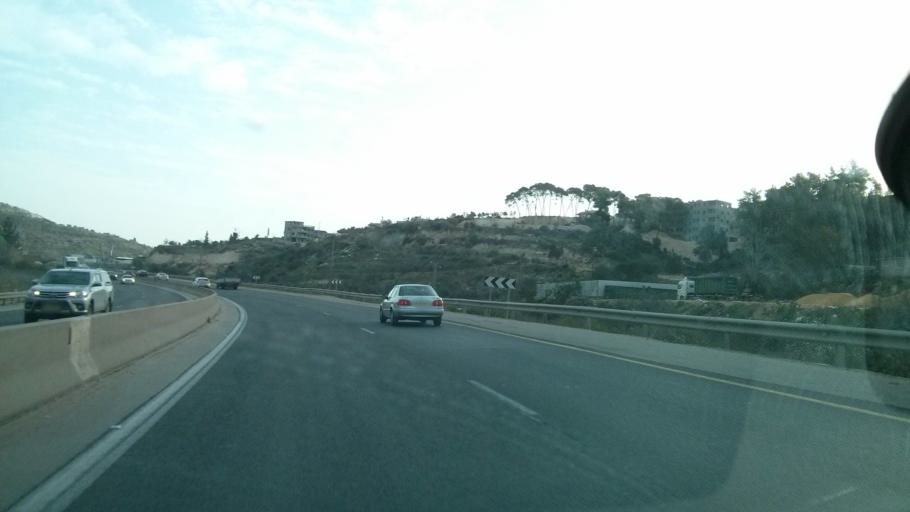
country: IL
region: Haifa
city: Umm el Fahm
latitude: 32.5187
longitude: 35.1256
